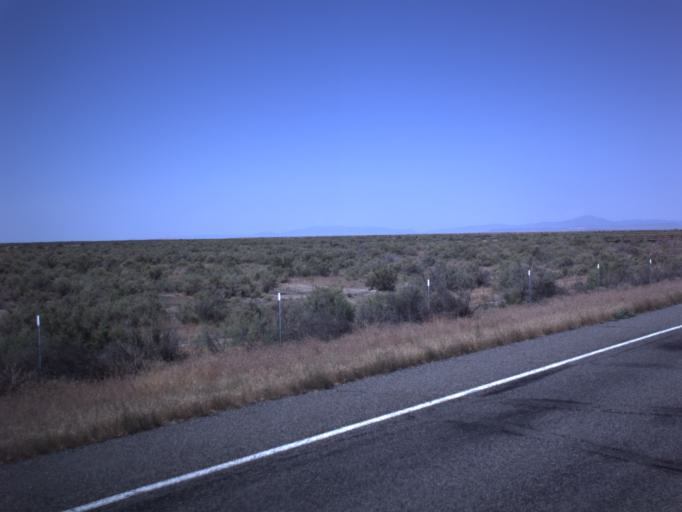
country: US
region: Utah
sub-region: Millard County
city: Delta
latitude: 39.4702
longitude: -112.4604
